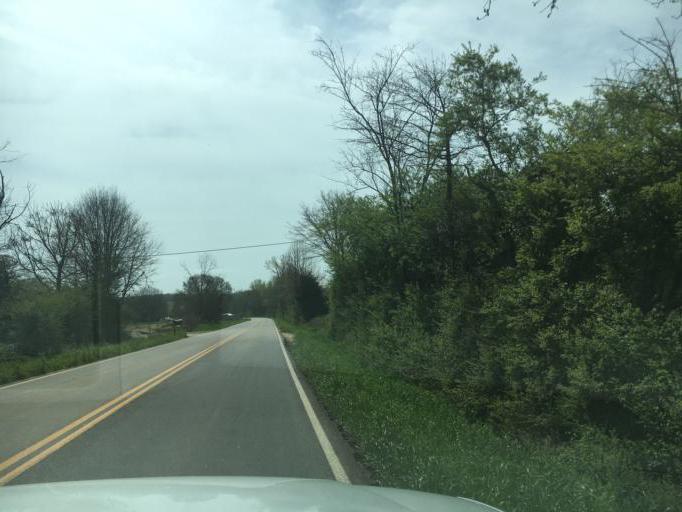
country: US
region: Georgia
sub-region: Franklin County
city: Lavonia
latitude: 34.3949
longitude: -83.0655
